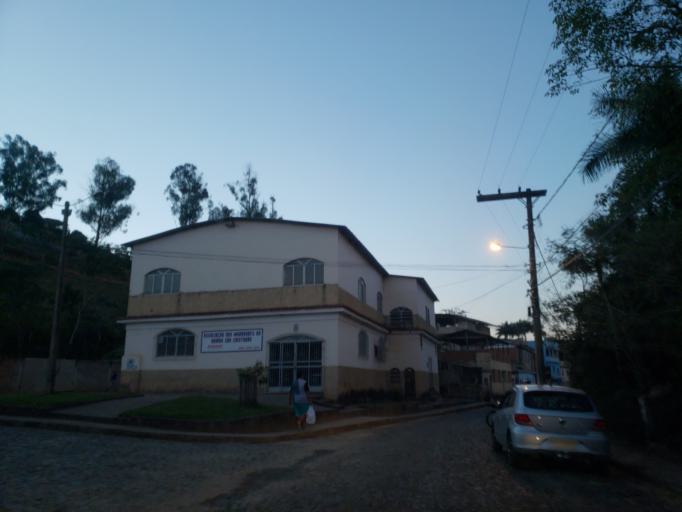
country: BR
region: Minas Gerais
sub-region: Sao Joao Nepomuceno
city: Sao Joao Nepomuceno
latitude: -21.5219
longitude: -43.0155
